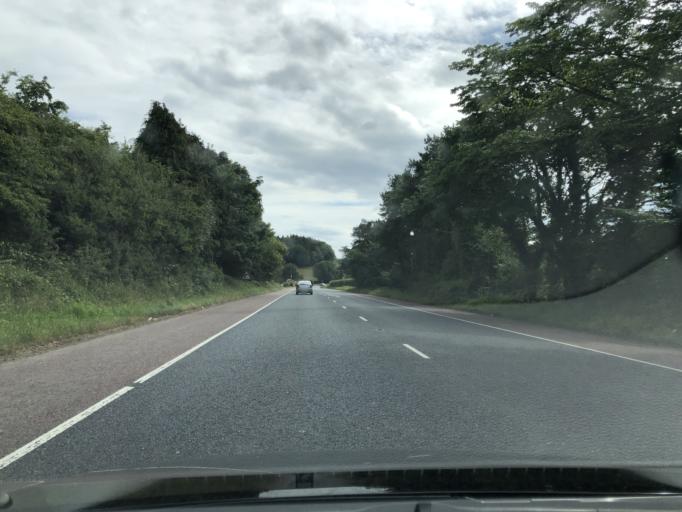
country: GB
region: Northern Ireland
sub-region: Down District
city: Dundrum
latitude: 54.3278
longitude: -5.8350
